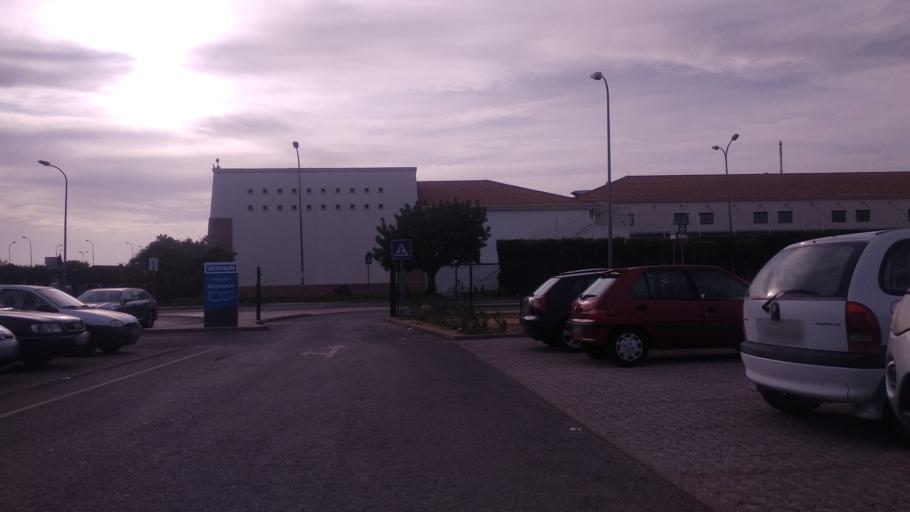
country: PT
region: Faro
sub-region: Faro
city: Faro
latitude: 37.0288
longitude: -7.9428
